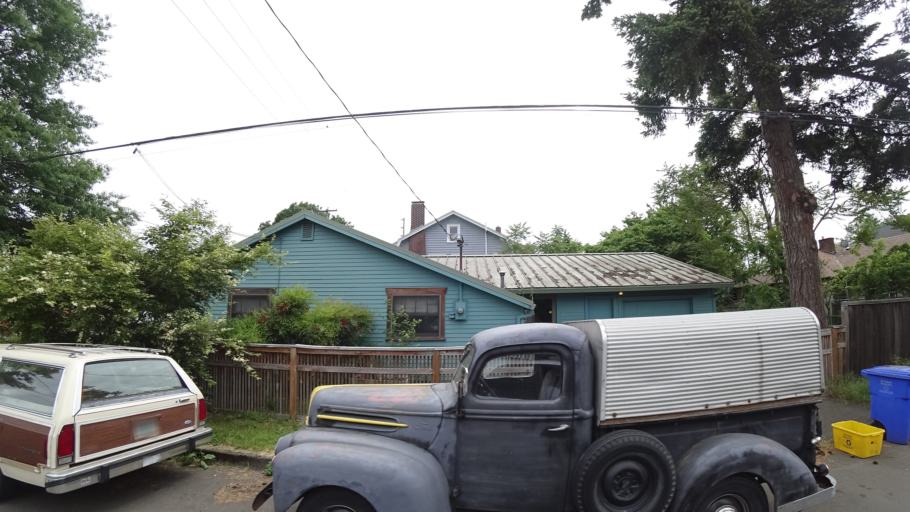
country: US
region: Oregon
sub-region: Multnomah County
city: Lents
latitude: 45.5309
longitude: -122.6041
